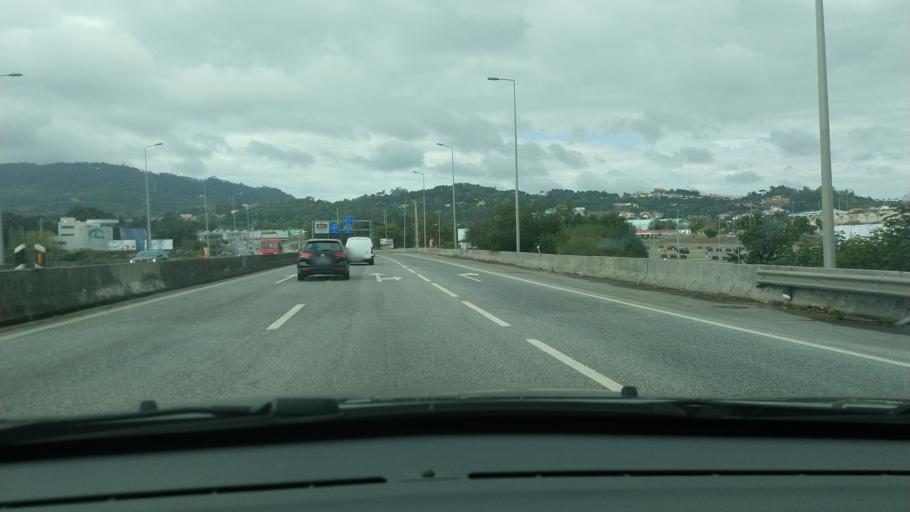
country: PT
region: Lisbon
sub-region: Sintra
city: Rio de Mouro
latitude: 38.7804
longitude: -9.3555
